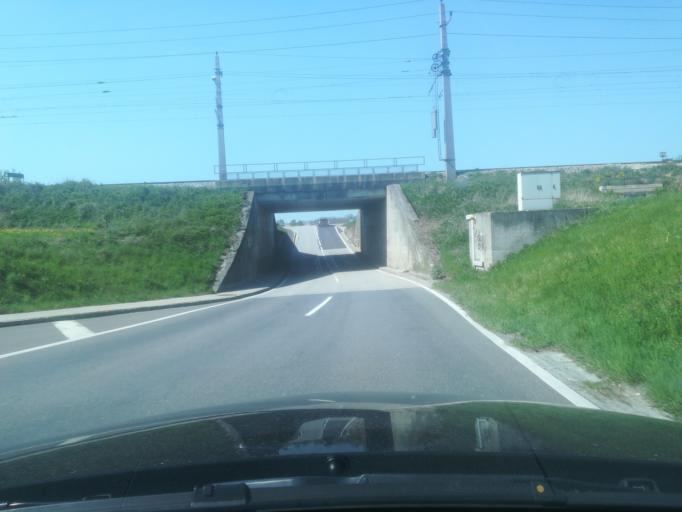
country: AT
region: Upper Austria
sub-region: Politischer Bezirk Linz-Land
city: Pasching
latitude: 48.2490
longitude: 14.1939
